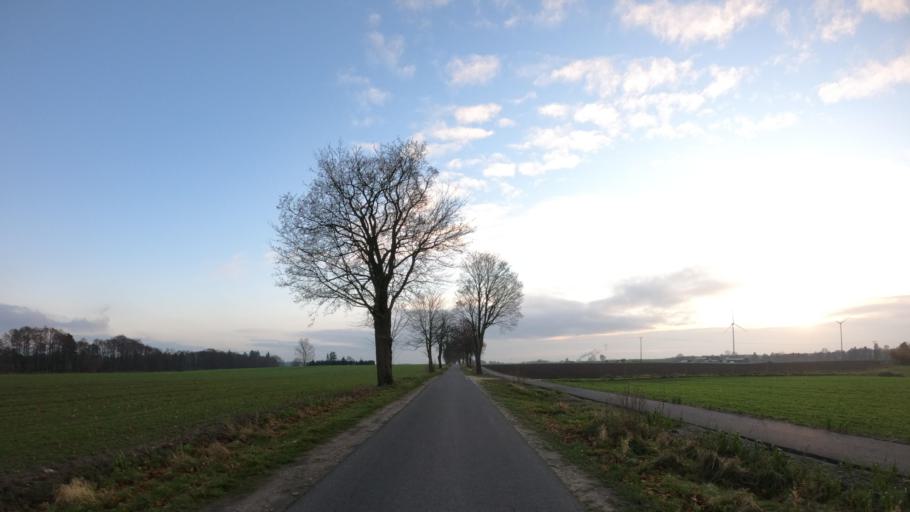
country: PL
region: West Pomeranian Voivodeship
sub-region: Powiat bialogardzki
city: Karlino
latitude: 54.1015
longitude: 15.8853
